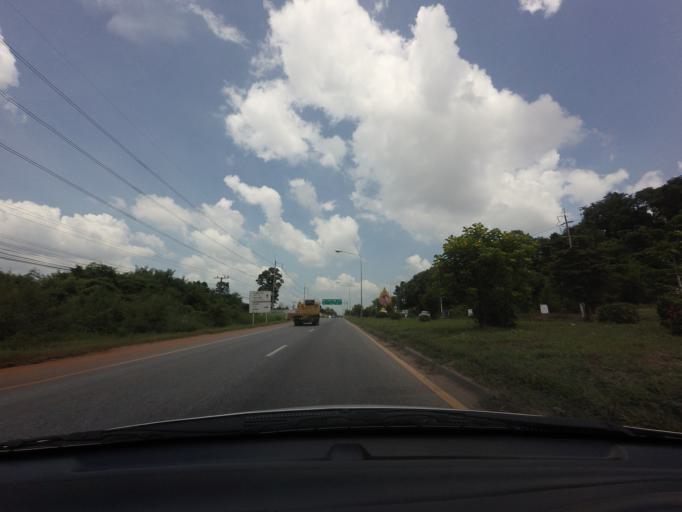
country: TH
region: Chachoengsao
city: Sanam Chai Khet
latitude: 13.7766
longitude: 101.5237
